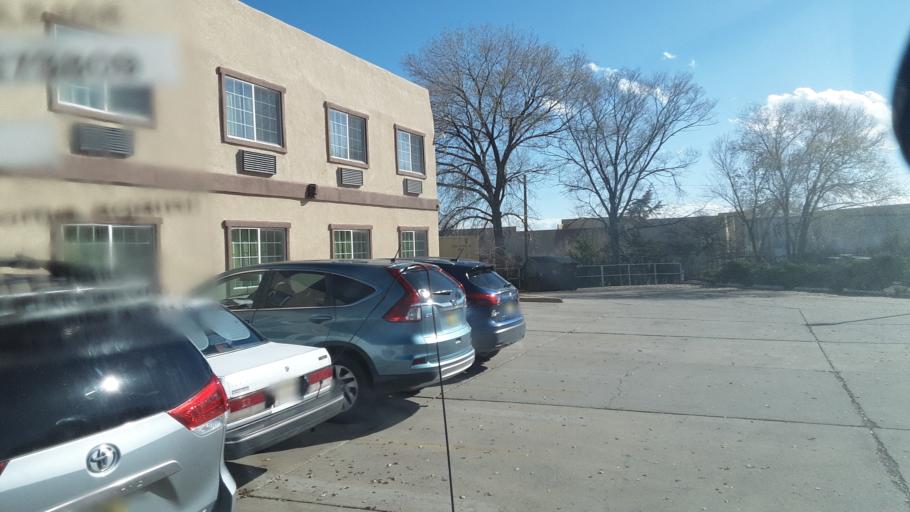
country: US
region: New Mexico
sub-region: Santa Fe County
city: Agua Fria
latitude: 35.6430
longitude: -106.0104
